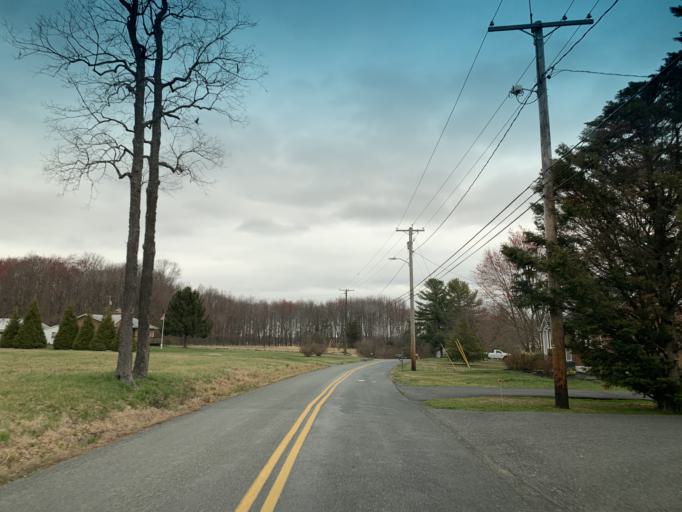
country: US
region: Maryland
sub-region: Harford County
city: Aberdeen
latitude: 39.5554
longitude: -76.1961
